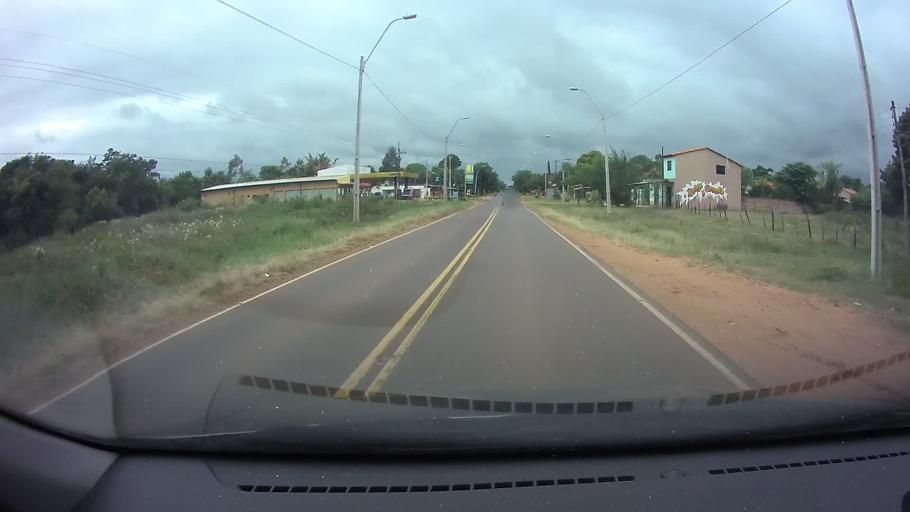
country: PY
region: Central
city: Nueva Italia
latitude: -25.6061
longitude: -57.4846
